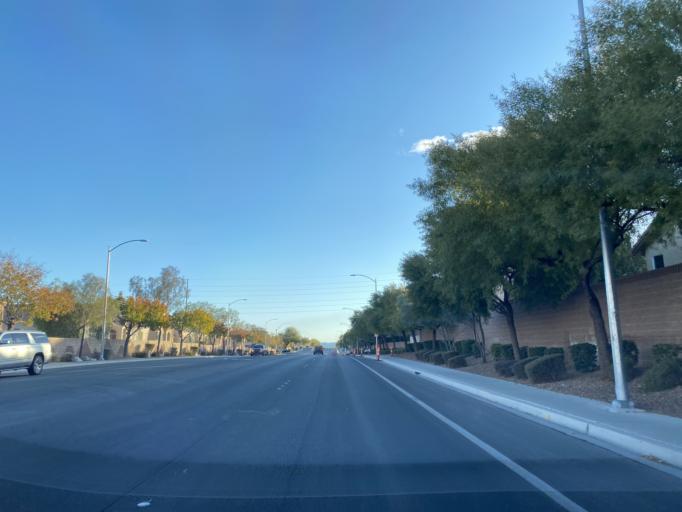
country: US
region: Nevada
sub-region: Clark County
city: Summerlin South
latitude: 36.3012
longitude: -115.3059
